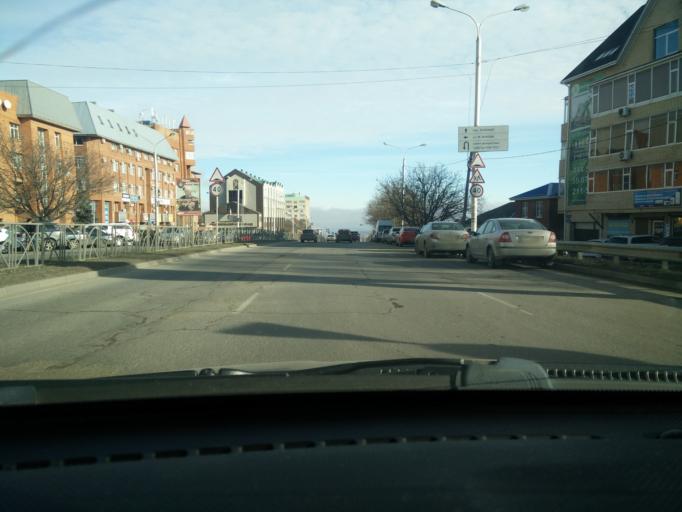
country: RU
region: Stavropol'skiy
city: Stavropol'
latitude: 45.0348
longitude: 41.9687
